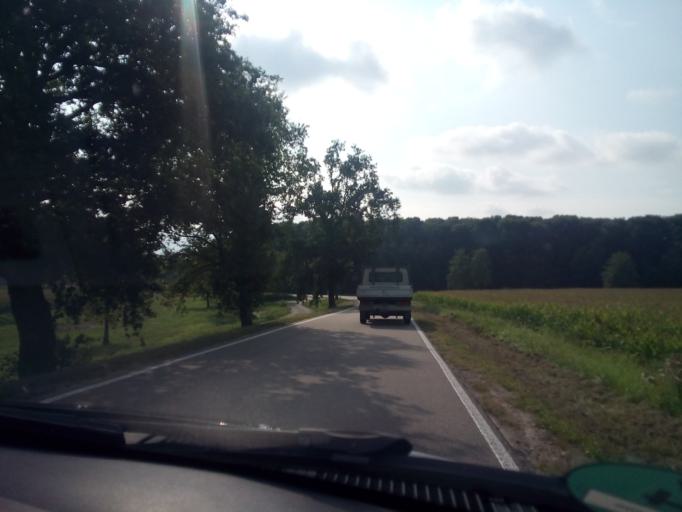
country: DE
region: Baden-Wuerttemberg
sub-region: Karlsruhe Region
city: Zell
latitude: 48.6594
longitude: 8.0401
